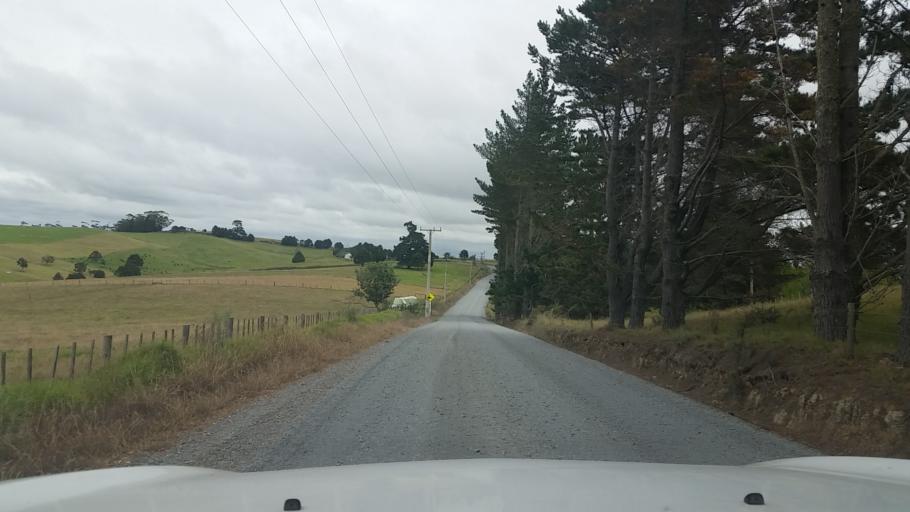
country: NZ
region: Northland
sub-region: Whangarei
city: Maungatapere
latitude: -35.6635
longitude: 174.1837
